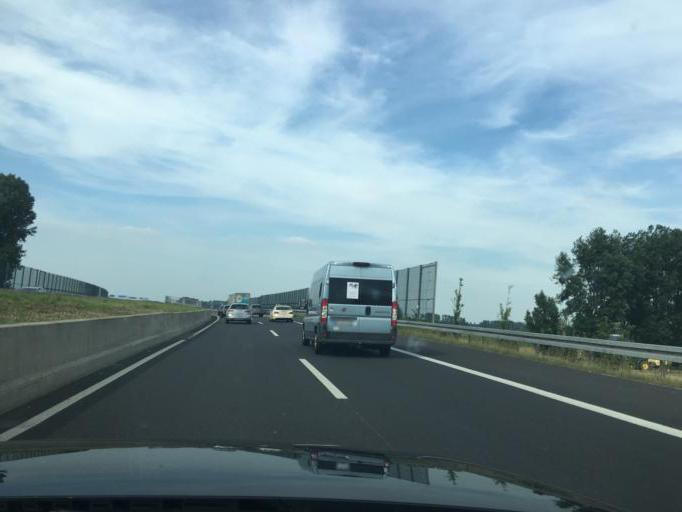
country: DE
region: North Rhine-Westphalia
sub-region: Regierungsbezirk Dusseldorf
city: Hochfeld
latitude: 51.3459
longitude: 6.7535
